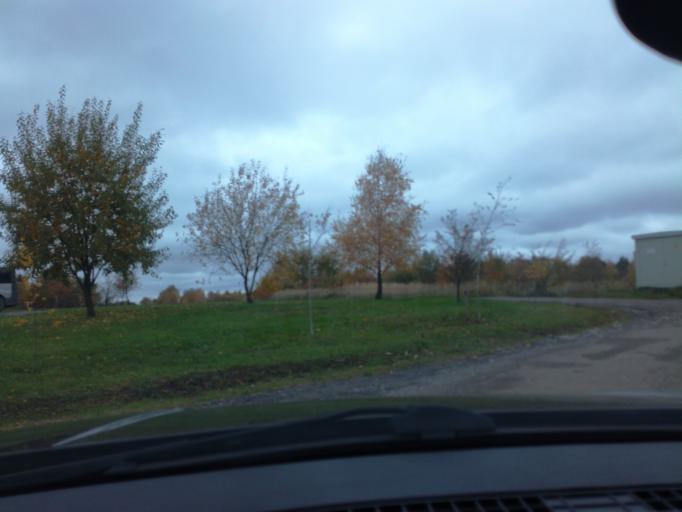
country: LT
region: Alytaus apskritis
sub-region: Alytus
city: Alytus
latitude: 54.4059
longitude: 24.0122
